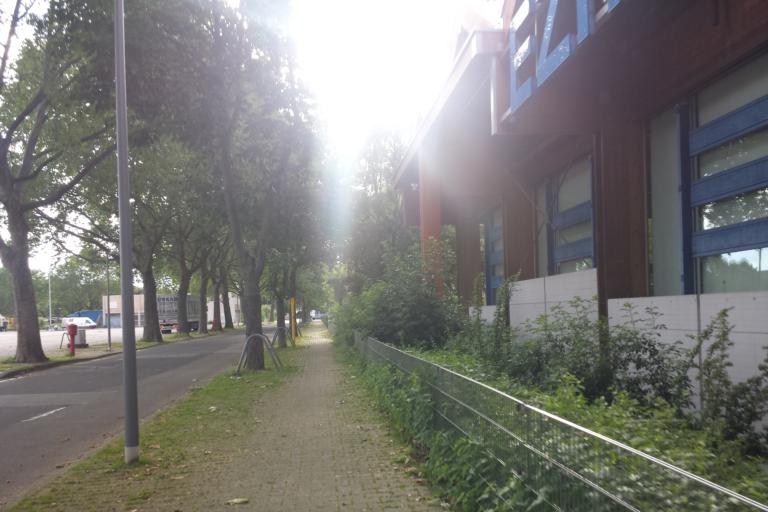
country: DE
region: Baden-Wuerttemberg
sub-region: Karlsruhe Region
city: Mannheim
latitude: 49.5057
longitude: 8.4756
